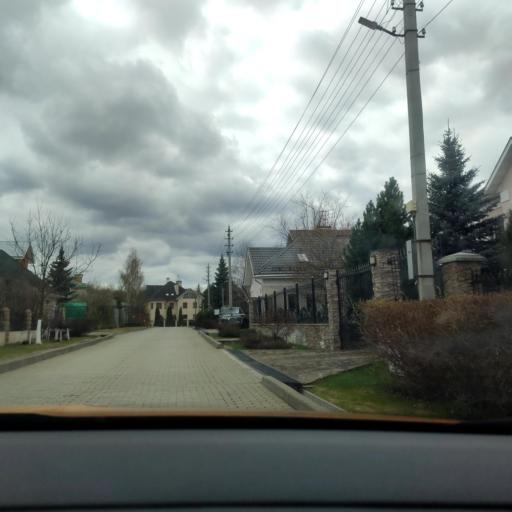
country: RU
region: Moskovskaya
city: Troitsk
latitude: 55.4996
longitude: 37.2277
